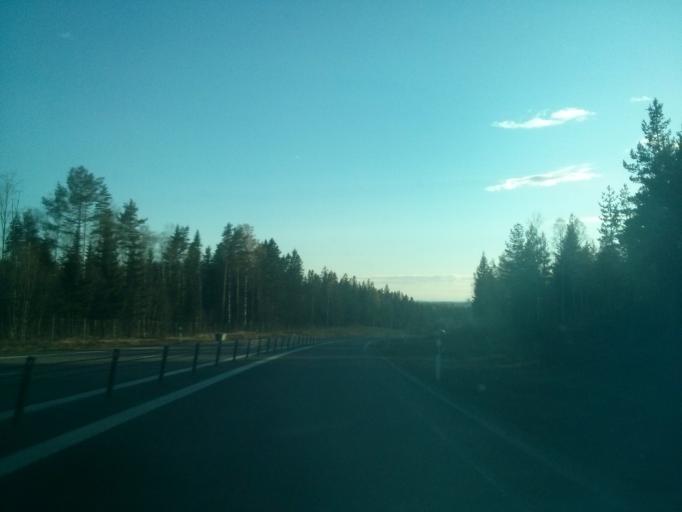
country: SE
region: Vaesternorrland
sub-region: Haernoesands Kommun
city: Haernoesand
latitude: 62.5636
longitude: 17.7282
